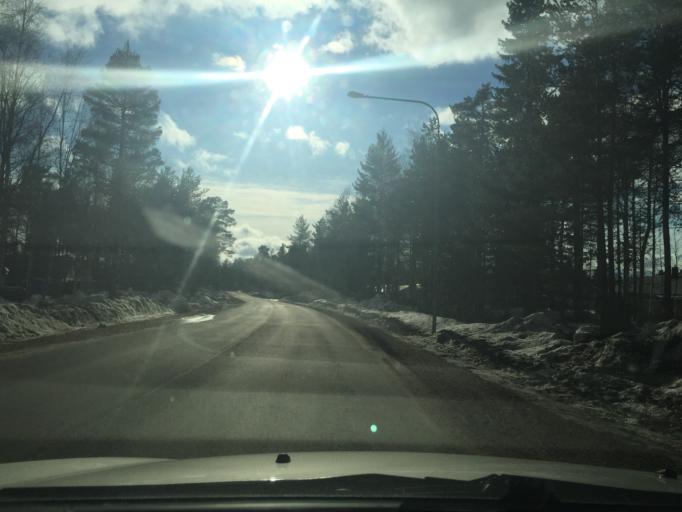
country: SE
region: Norrbotten
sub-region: Lulea Kommun
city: Lulea
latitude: 65.5943
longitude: 22.2343
